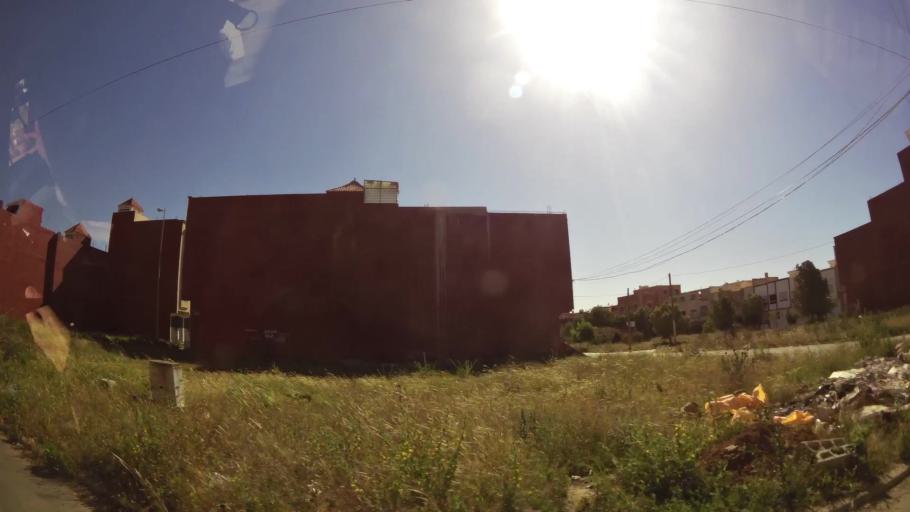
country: MA
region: Oriental
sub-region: Berkane-Taourirt
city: Berkane
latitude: 34.9452
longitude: -2.3340
